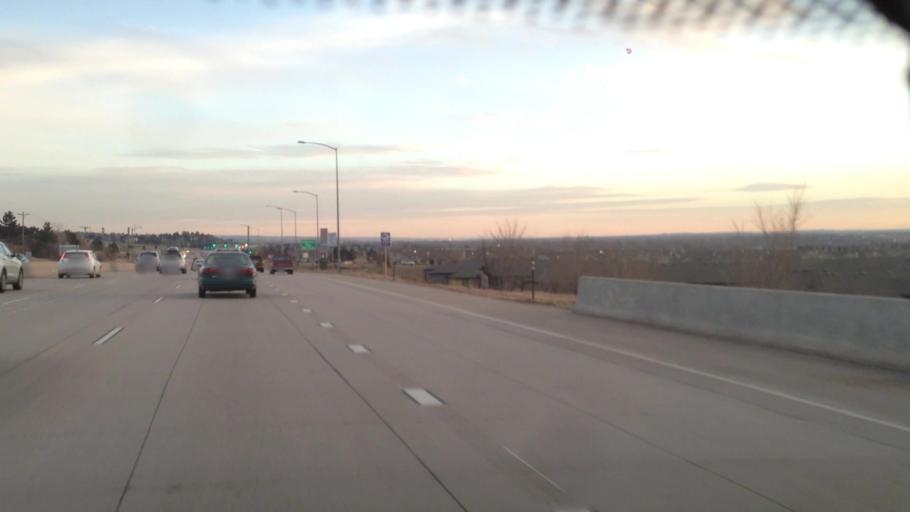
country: US
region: Colorado
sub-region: Arapahoe County
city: Dove Valley
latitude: 39.5906
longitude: -104.7999
